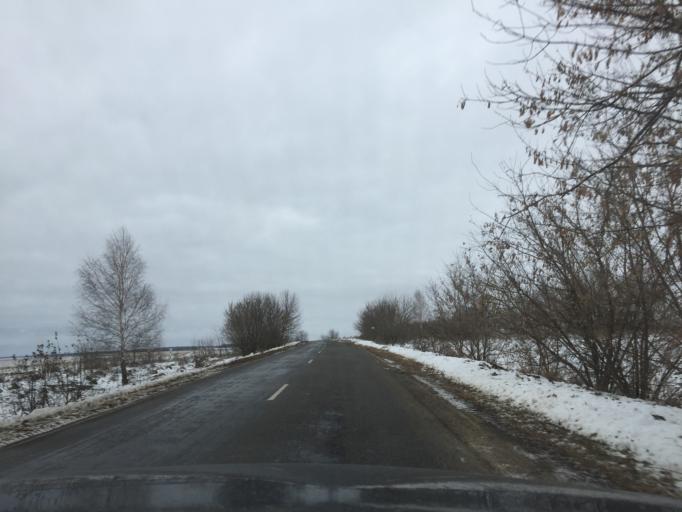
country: RU
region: Tula
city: Teploye
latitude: 53.8011
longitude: 37.5872
